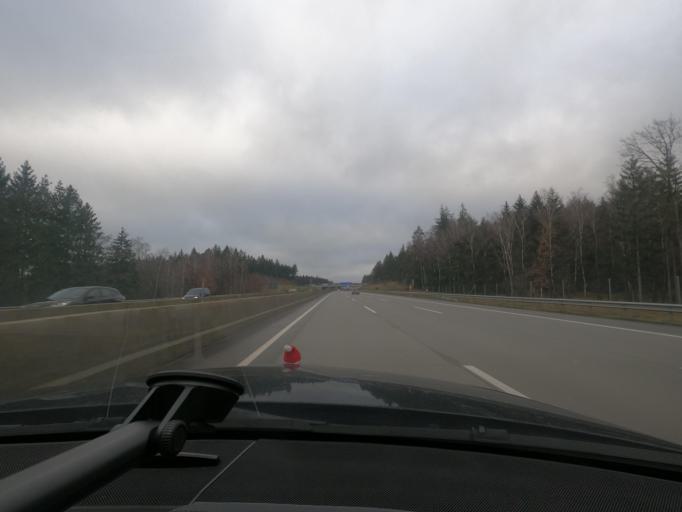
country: DE
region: Schleswig-Holstein
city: Schmalfeld
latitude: 53.8948
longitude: 9.9400
